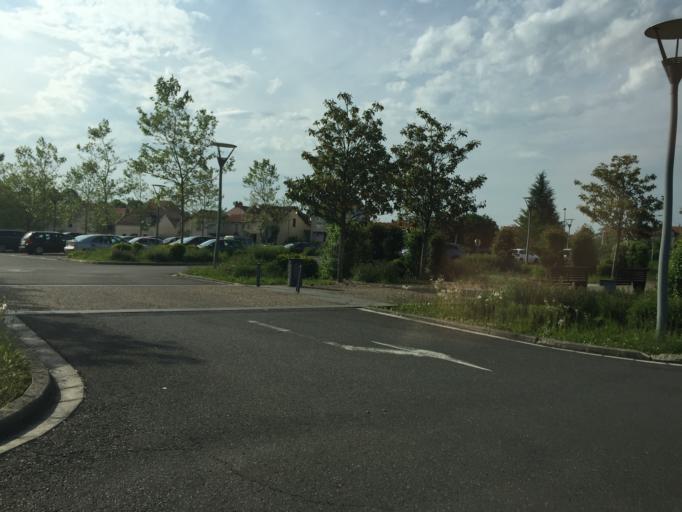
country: FR
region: Auvergne
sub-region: Departement de l'Allier
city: Vichy
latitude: 46.1242
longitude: 3.4371
